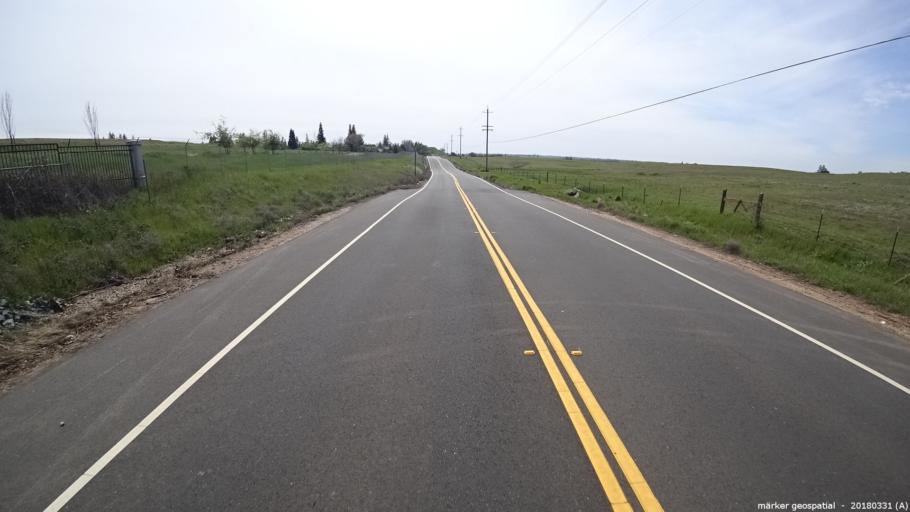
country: US
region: California
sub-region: Sacramento County
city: Rancho Murieta
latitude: 38.5065
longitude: -121.1019
